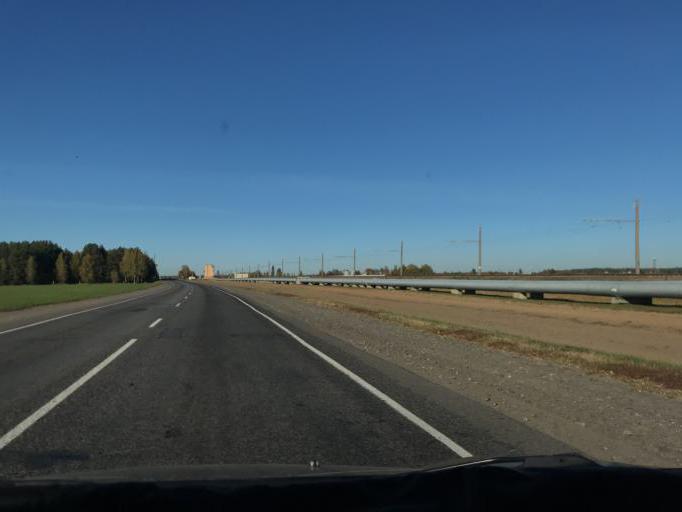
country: BY
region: Gomel
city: Mazyr
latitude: 51.9914
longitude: 29.2591
